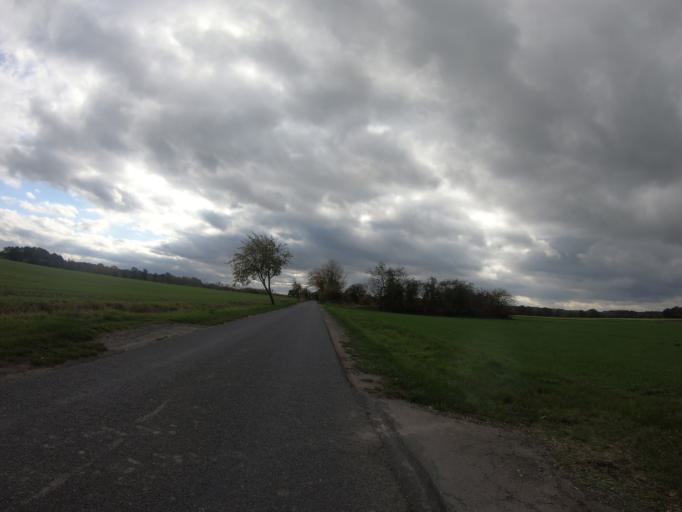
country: DE
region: Lower Saxony
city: Ribbesbuttel
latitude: 52.4210
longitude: 10.4829
